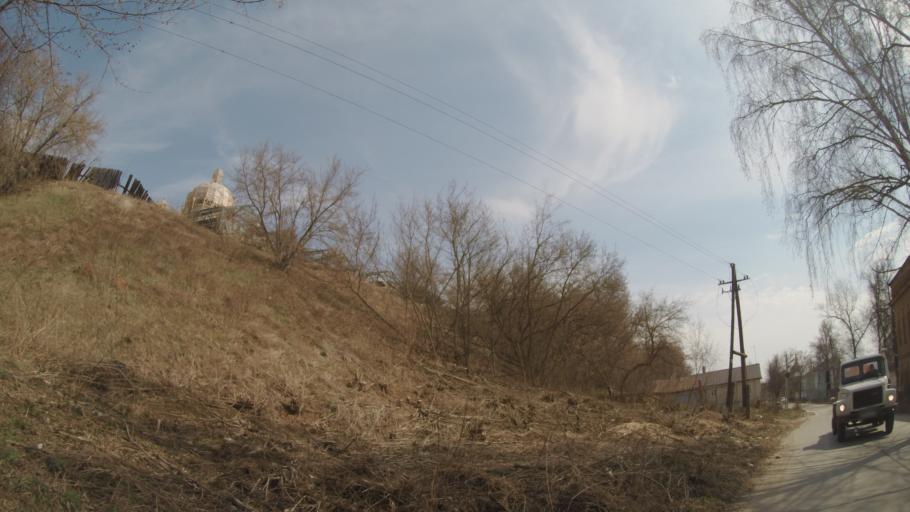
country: RU
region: Nizjnij Novgorod
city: Vyyezdnoye
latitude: 55.3859
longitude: 43.8117
